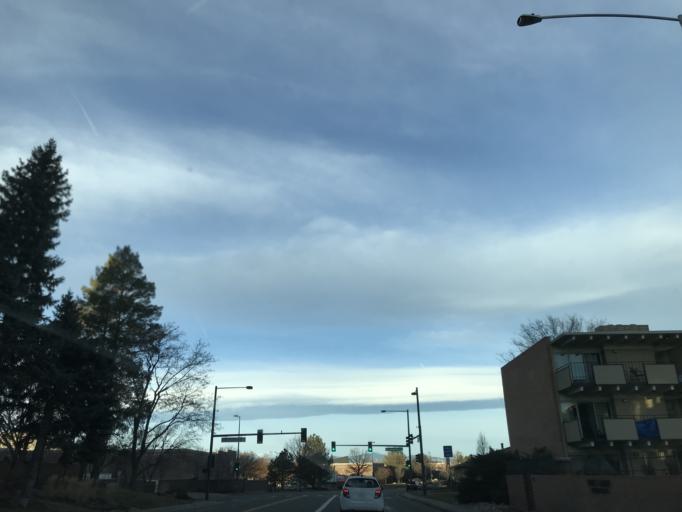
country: US
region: Colorado
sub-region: Arapahoe County
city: Cherry Hills Village
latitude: 39.6675
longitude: -104.9353
